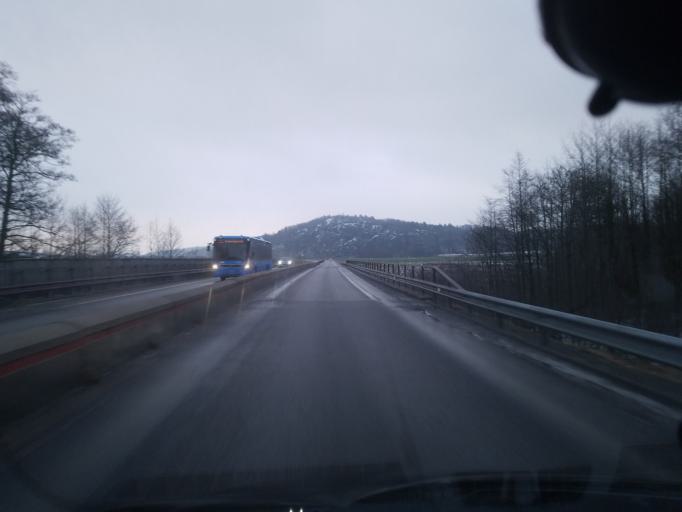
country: SE
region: Vaestra Goetaland
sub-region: Orust
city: Henan
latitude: 58.3488
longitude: 11.7472
